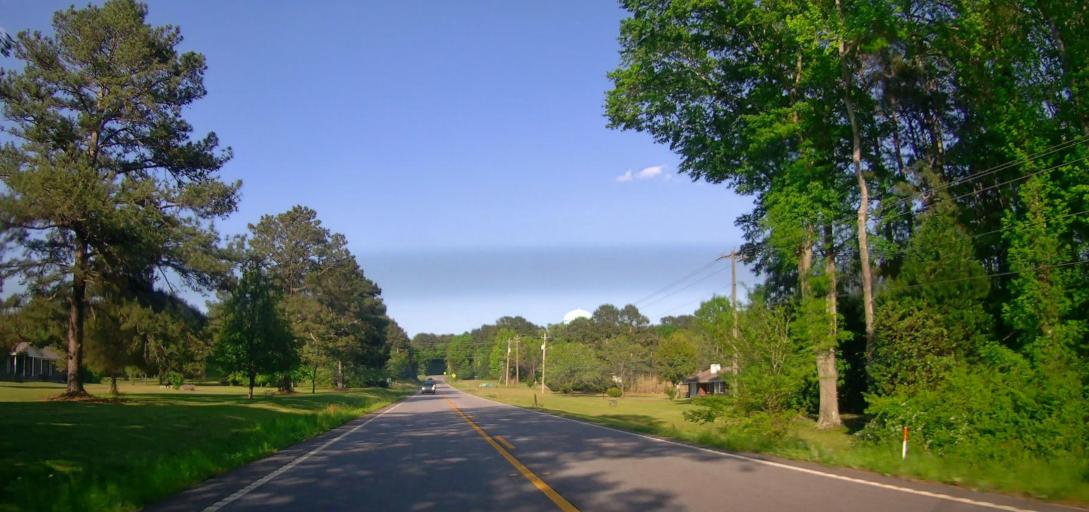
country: US
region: Georgia
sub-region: Newton County
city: Covington
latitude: 33.5970
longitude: -83.7809
